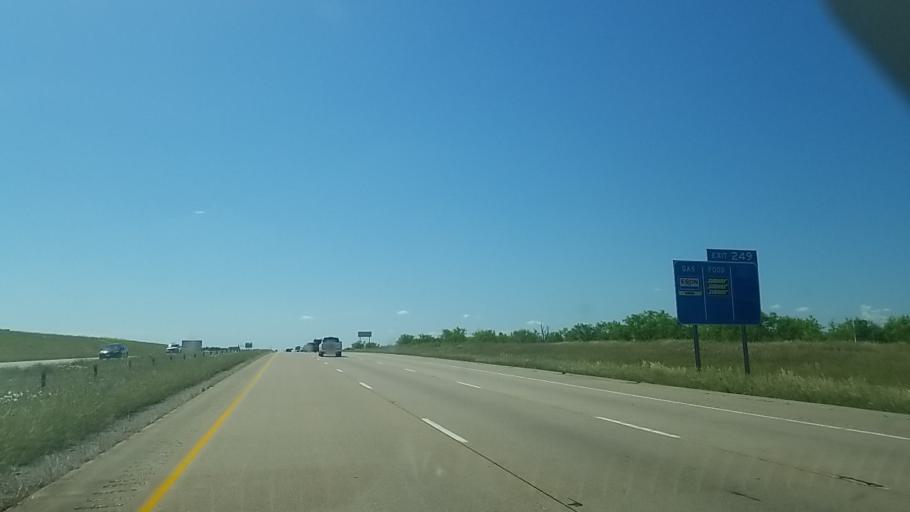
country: US
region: Texas
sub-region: Ellis County
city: Ennis
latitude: 32.2984
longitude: -96.5706
